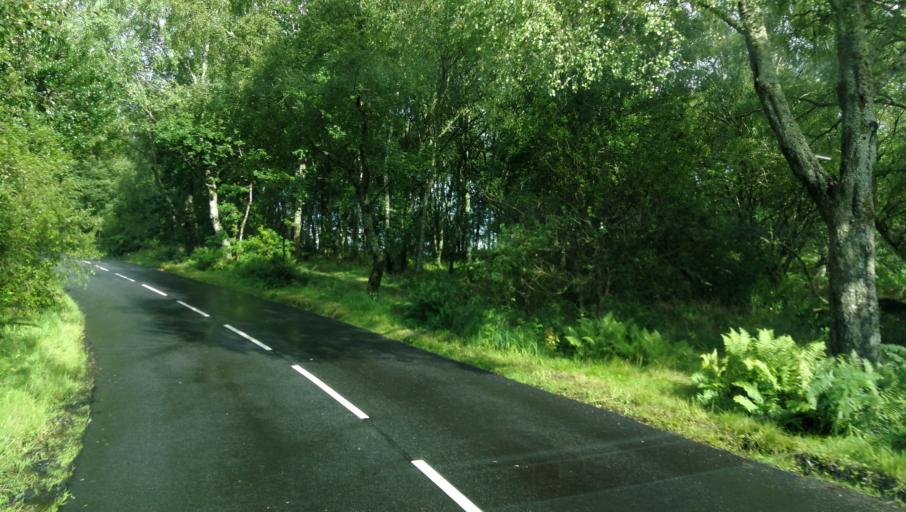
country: GB
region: Scotland
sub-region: Stirling
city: Callander
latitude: 56.2290
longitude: -4.3592
